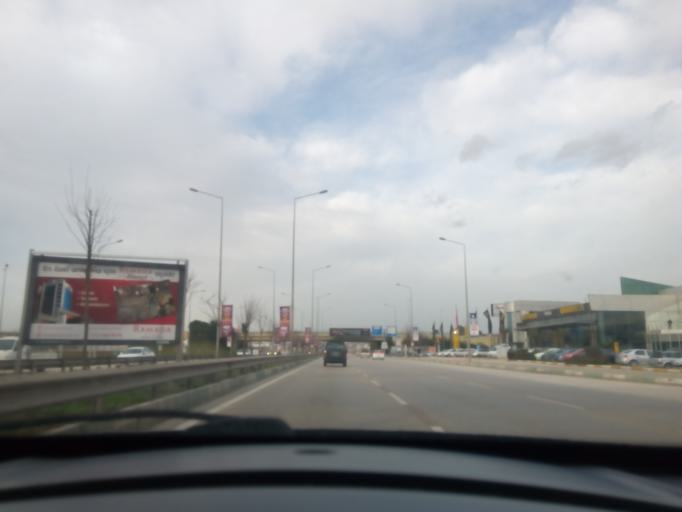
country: TR
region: Bursa
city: Cali
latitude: 40.2136
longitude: 28.9177
